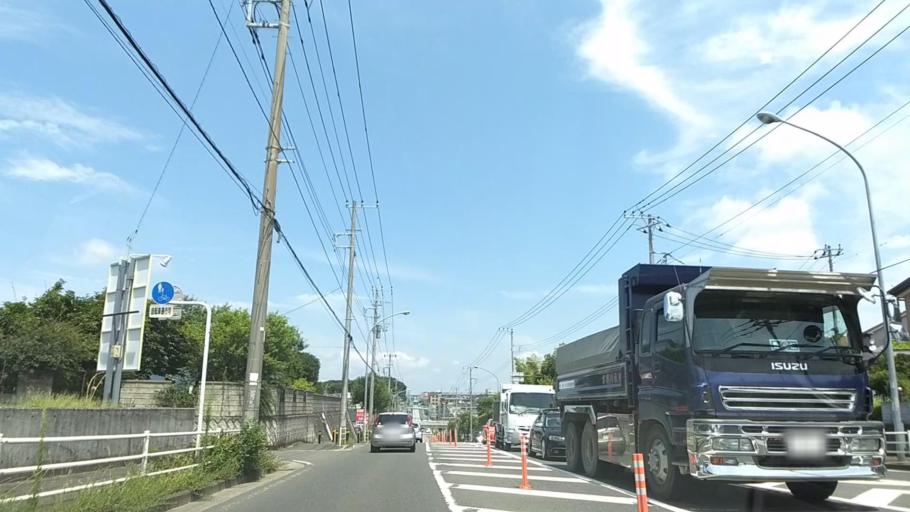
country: JP
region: Kanagawa
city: Minami-rinkan
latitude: 35.4505
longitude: 139.4835
